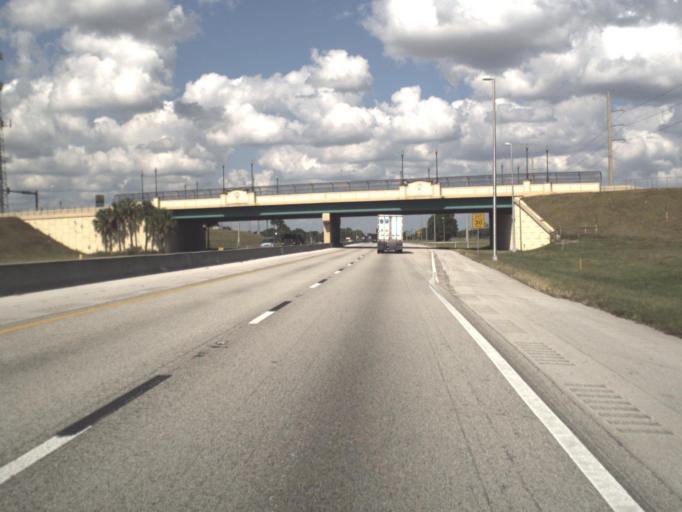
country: US
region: Florida
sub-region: Martin County
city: North River Shores
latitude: 27.2082
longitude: -80.3329
